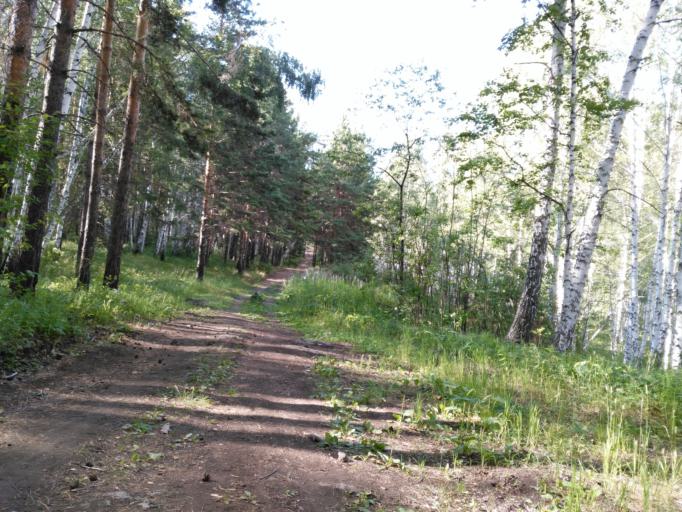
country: RU
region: Bashkortostan
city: Uchaly
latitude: 54.3326
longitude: 59.3574
